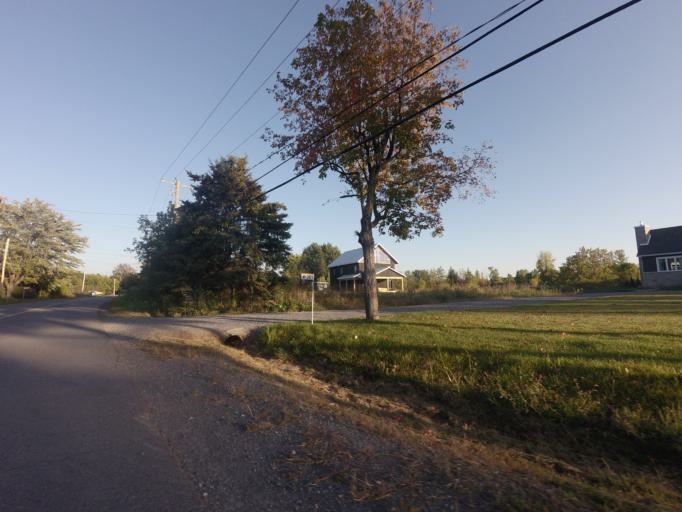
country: CA
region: Quebec
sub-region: Monteregie
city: Rigaud
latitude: 45.4807
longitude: -74.2481
